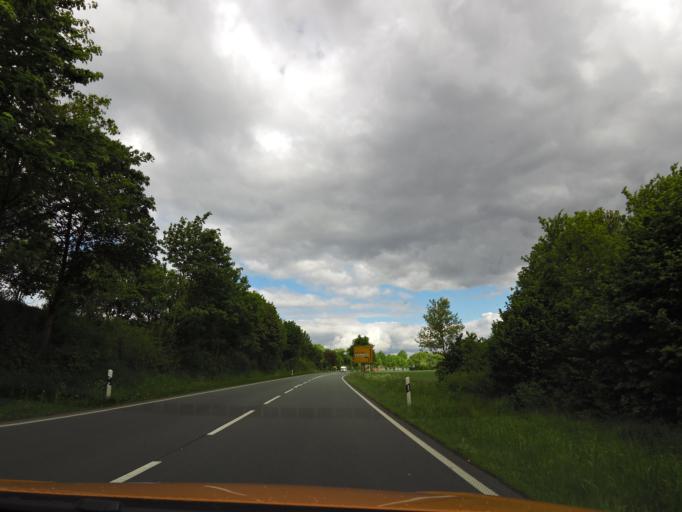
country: DE
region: Lower Saxony
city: Bassum
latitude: 52.8696
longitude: 8.7298
